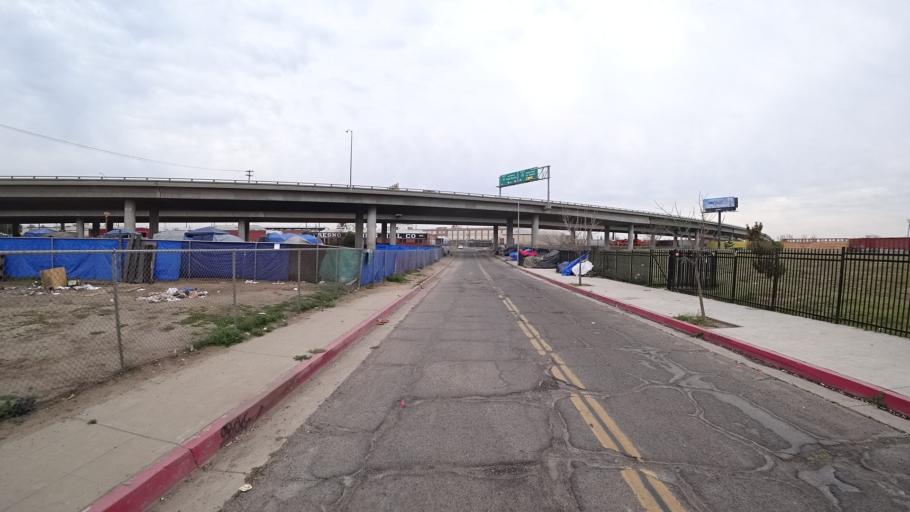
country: US
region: California
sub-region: Fresno County
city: Fresno
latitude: 36.7262
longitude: -119.7854
